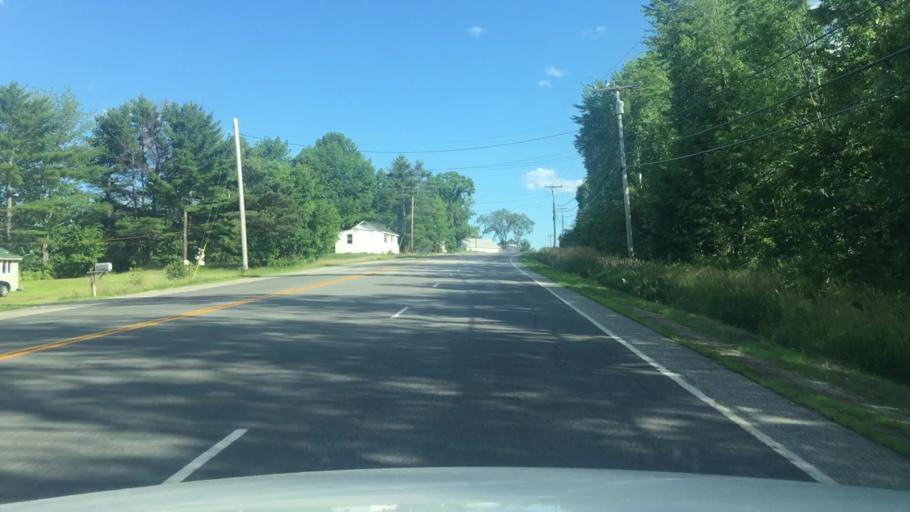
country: US
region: Maine
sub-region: Franklin County
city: Jay
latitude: 44.5211
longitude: -70.2256
